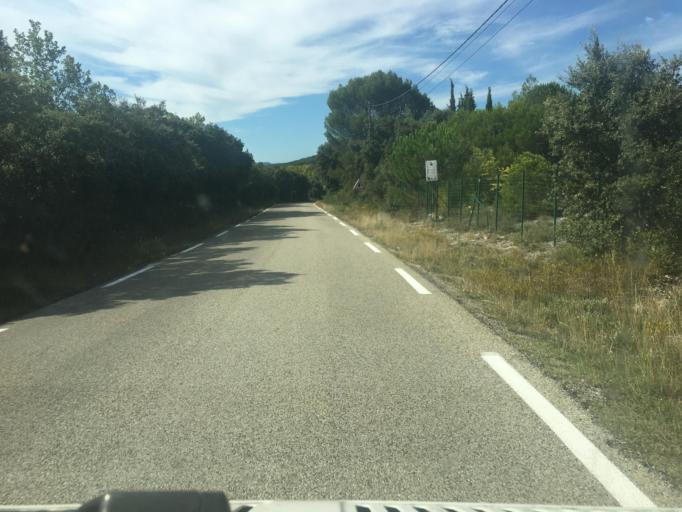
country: FR
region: Languedoc-Roussillon
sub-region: Departement du Gard
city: Saint-Quentin-la-Poterie
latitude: 44.0299
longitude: 4.4974
